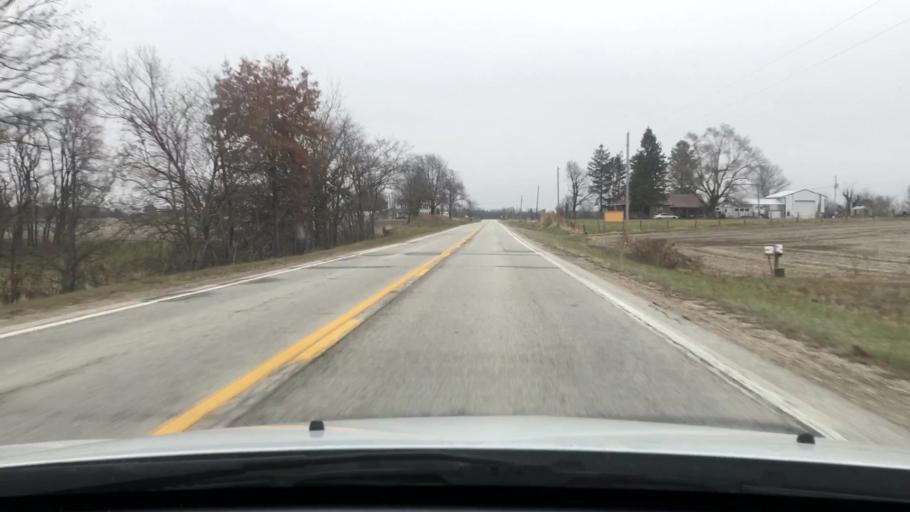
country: US
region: Illinois
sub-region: Pike County
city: Pittsfield
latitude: 39.5832
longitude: -90.9014
